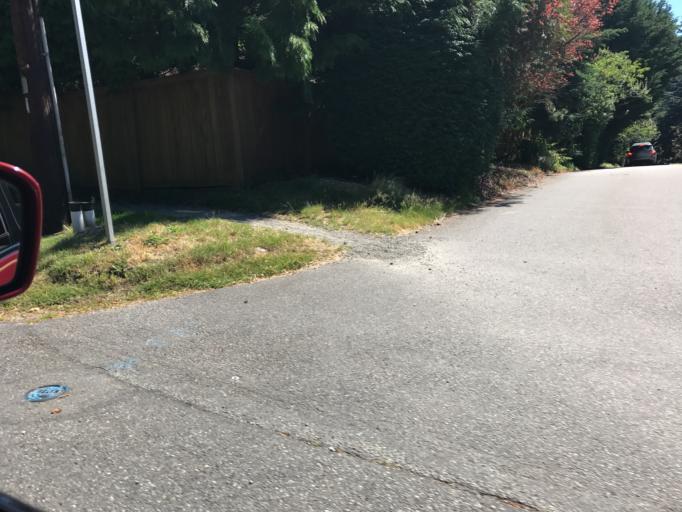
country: US
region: Washington
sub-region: King County
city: Bellevue
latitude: 47.6341
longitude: -122.1621
